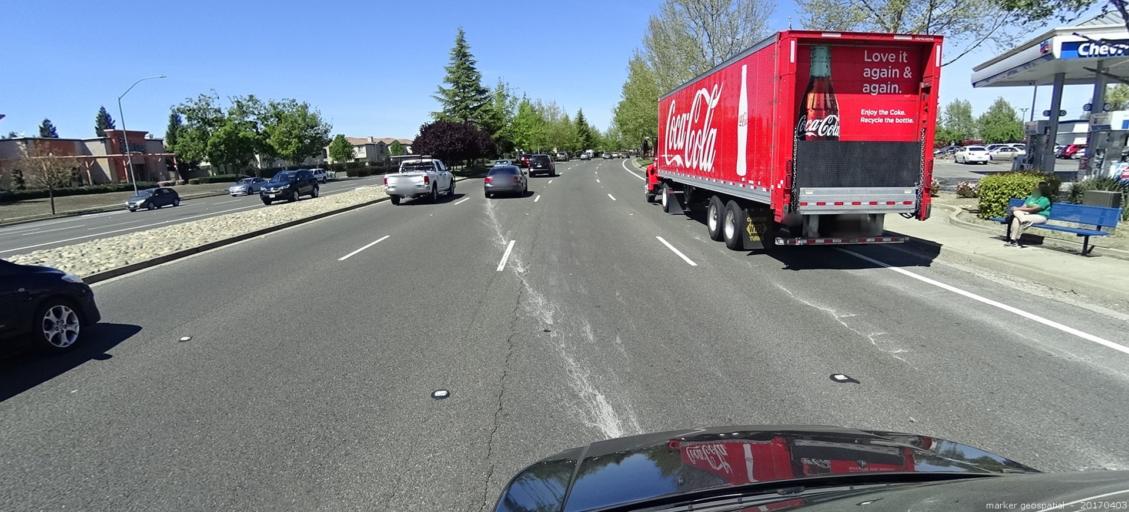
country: US
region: California
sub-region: Sacramento County
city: Sacramento
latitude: 38.6407
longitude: -121.5081
